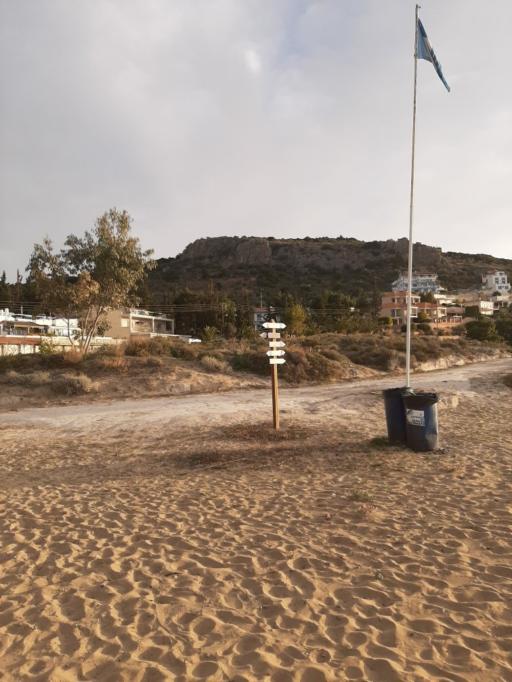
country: GR
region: Peloponnese
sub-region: Nomos Argolidos
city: Tolon
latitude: 37.5269
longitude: 22.8667
